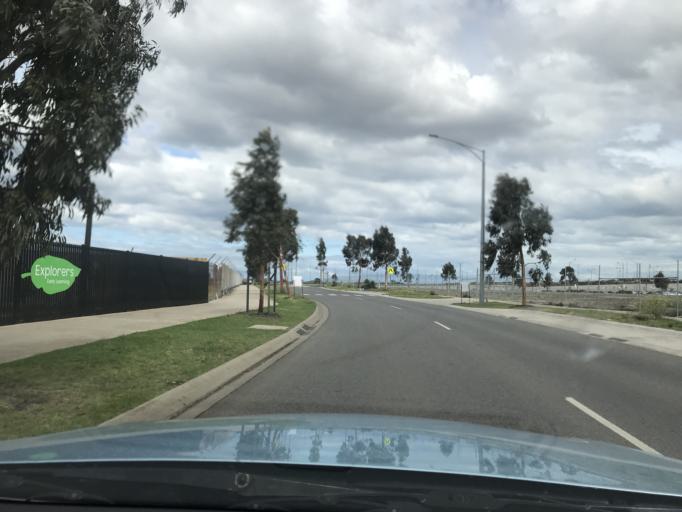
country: AU
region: Victoria
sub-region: Wyndham
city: Williams Landing
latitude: -37.8668
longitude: 144.7503
